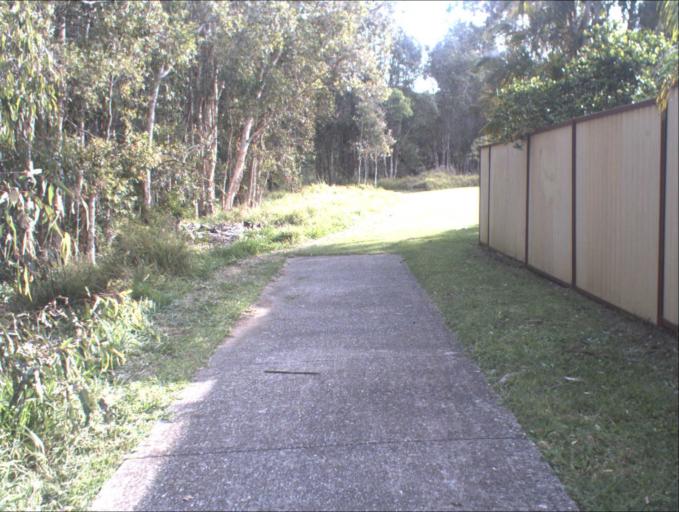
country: AU
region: Queensland
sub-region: Logan
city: Park Ridge South
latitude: -27.6806
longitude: 153.0335
